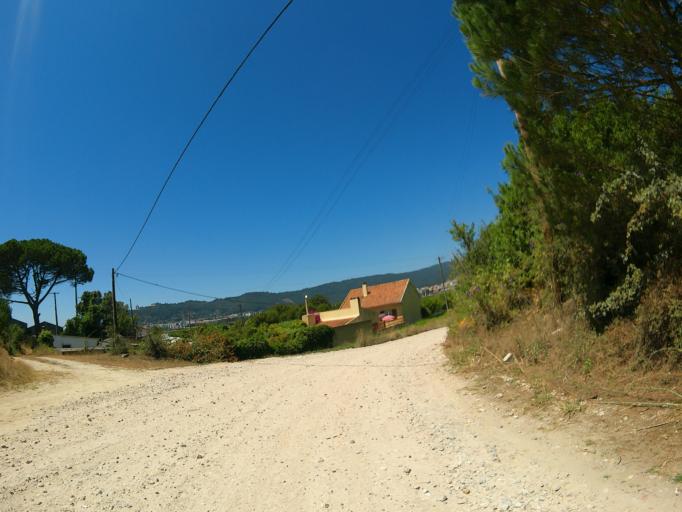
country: PT
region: Viana do Castelo
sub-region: Viana do Castelo
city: Meadela
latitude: 41.6866
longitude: -8.8042
